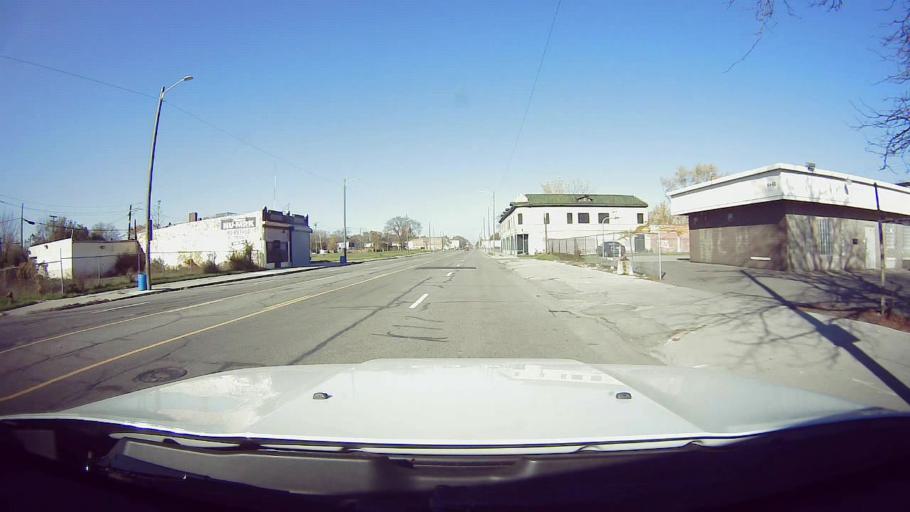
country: US
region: Michigan
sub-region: Wayne County
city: Highland Park
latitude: 42.3693
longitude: -83.1059
